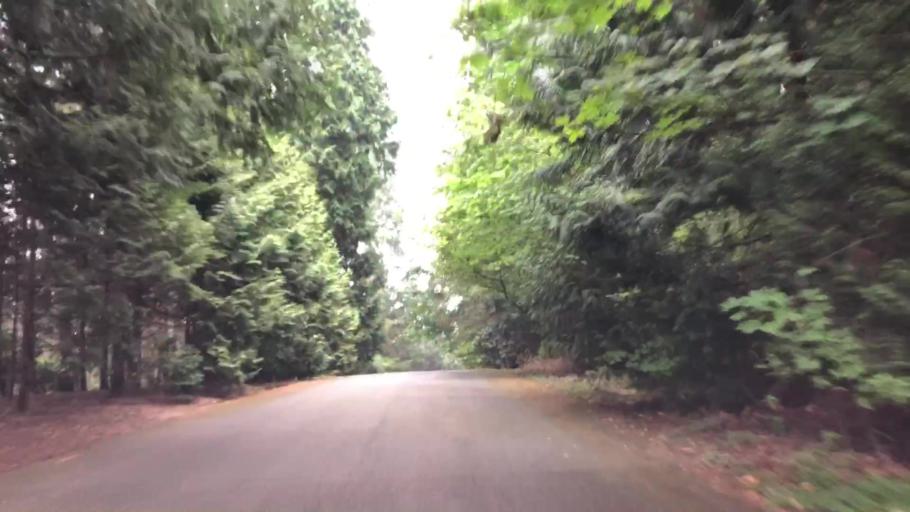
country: US
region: Washington
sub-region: King County
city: Cottage Lake
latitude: 47.7378
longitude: -122.1068
